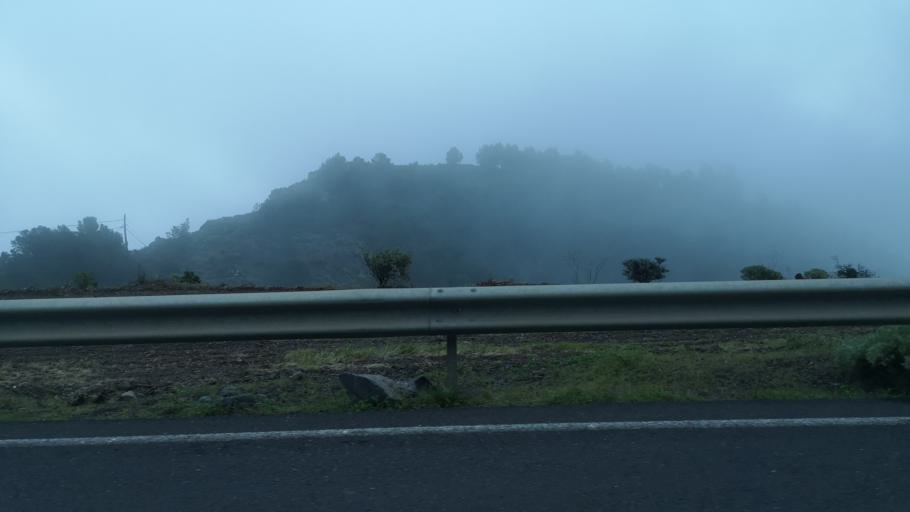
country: ES
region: Canary Islands
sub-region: Provincia de Santa Cruz de Tenerife
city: Alajero
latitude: 28.0880
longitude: -17.1998
